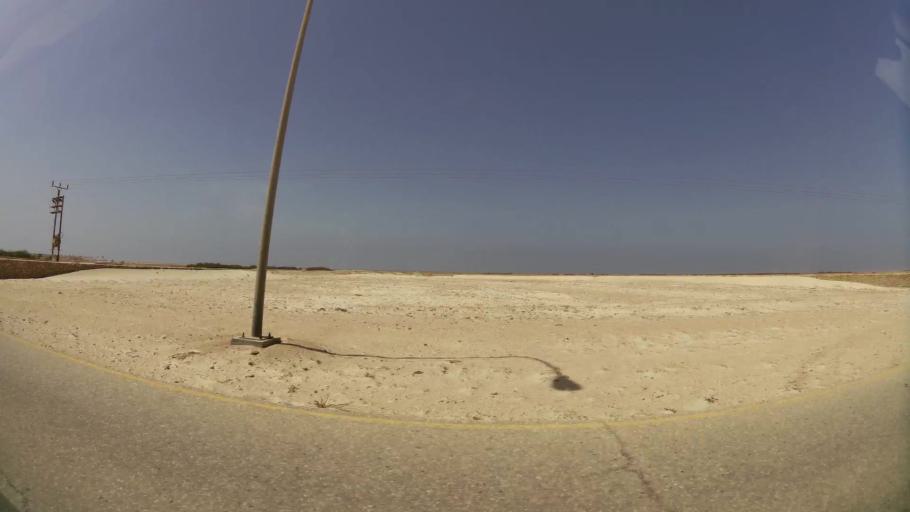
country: OM
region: Zufar
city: Salalah
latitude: 17.0380
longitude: 54.2803
